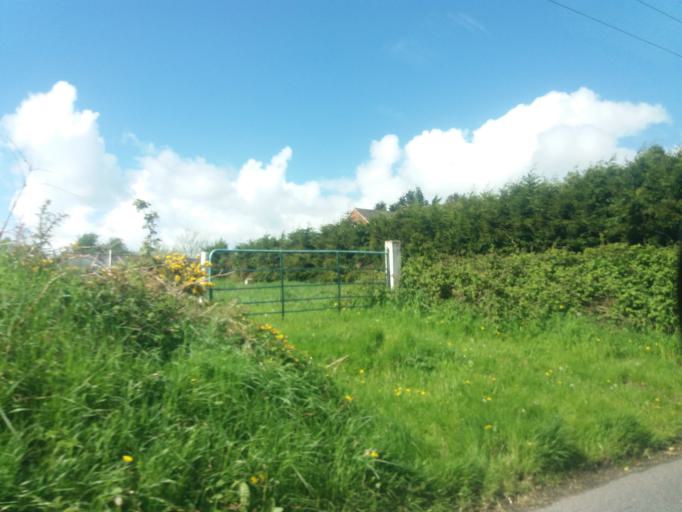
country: IE
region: Leinster
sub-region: Loch Garman
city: Castlebridge
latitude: 52.3922
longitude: -6.3874
